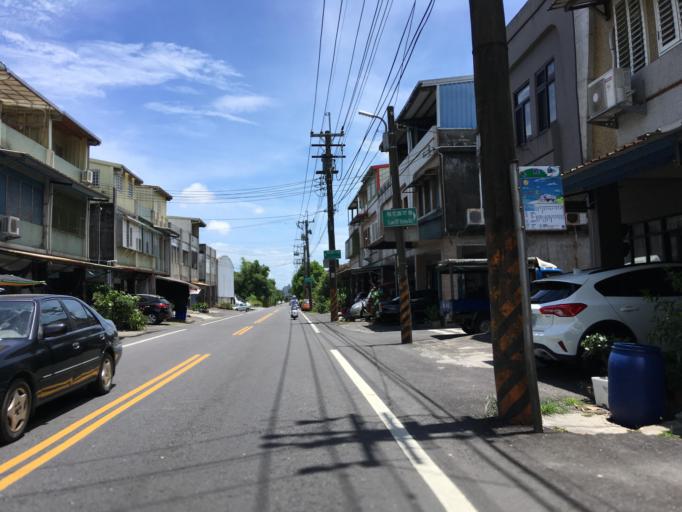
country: TW
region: Taiwan
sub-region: Yilan
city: Yilan
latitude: 24.6601
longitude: 121.7354
